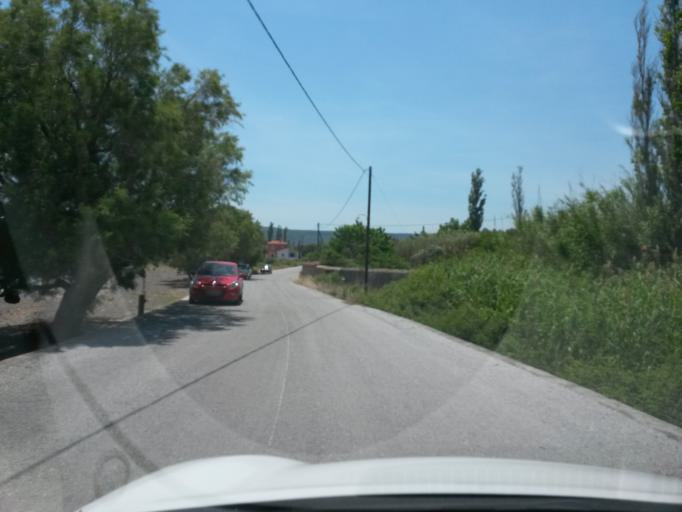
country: GR
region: North Aegean
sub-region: Nomos Lesvou
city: Mantamados
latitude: 39.2933
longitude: 26.3883
